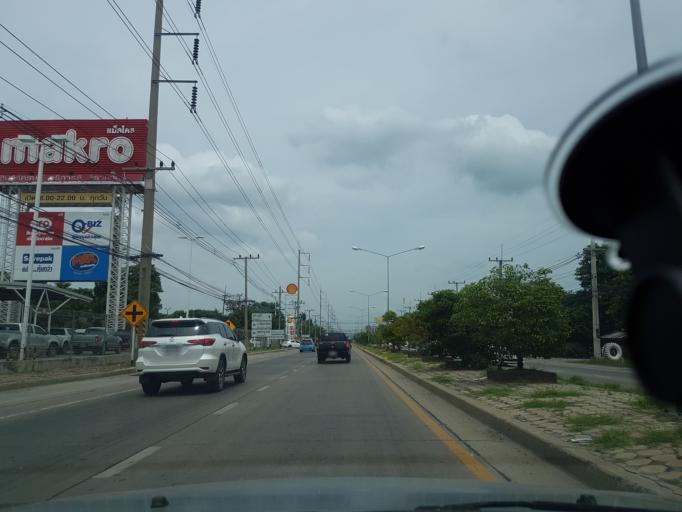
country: TH
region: Lop Buri
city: Lop Buri
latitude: 14.7818
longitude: 100.6861
